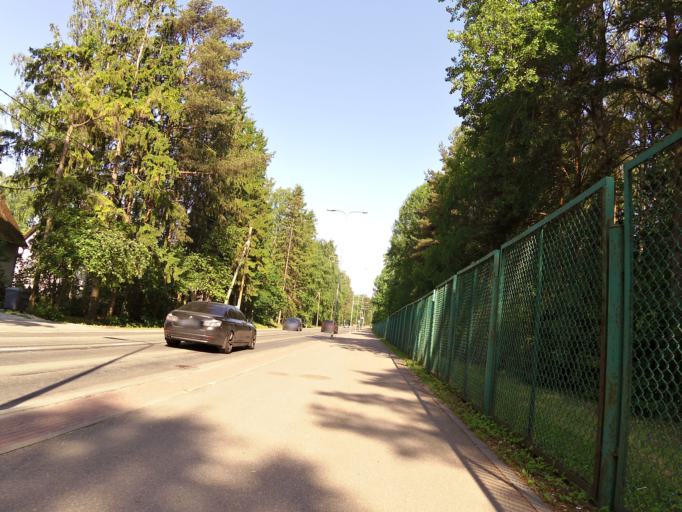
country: EE
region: Harju
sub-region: Saue vald
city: Laagri
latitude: 59.4323
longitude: 24.6338
